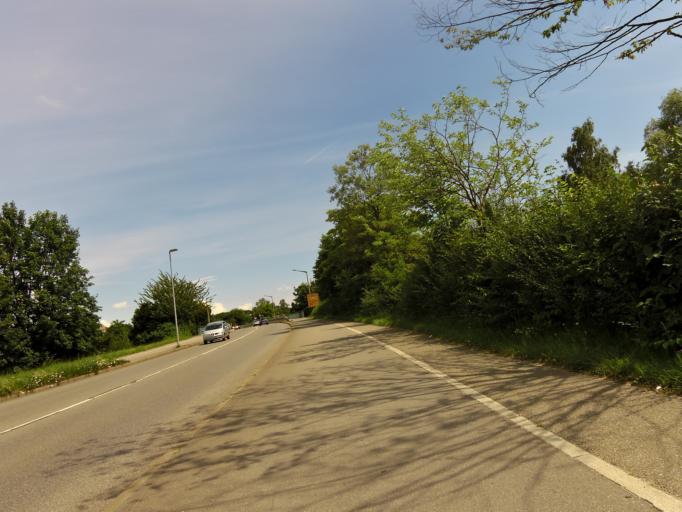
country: DE
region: Baden-Wuerttemberg
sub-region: Tuebingen Region
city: Friedrichshafen
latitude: 47.6650
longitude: 9.4269
